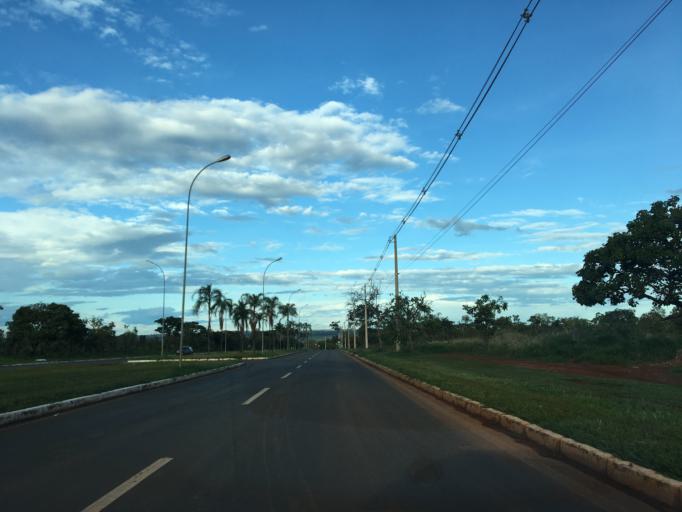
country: BR
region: Federal District
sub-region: Brasilia
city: Brasilia
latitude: -15.8091
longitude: -47.8414
